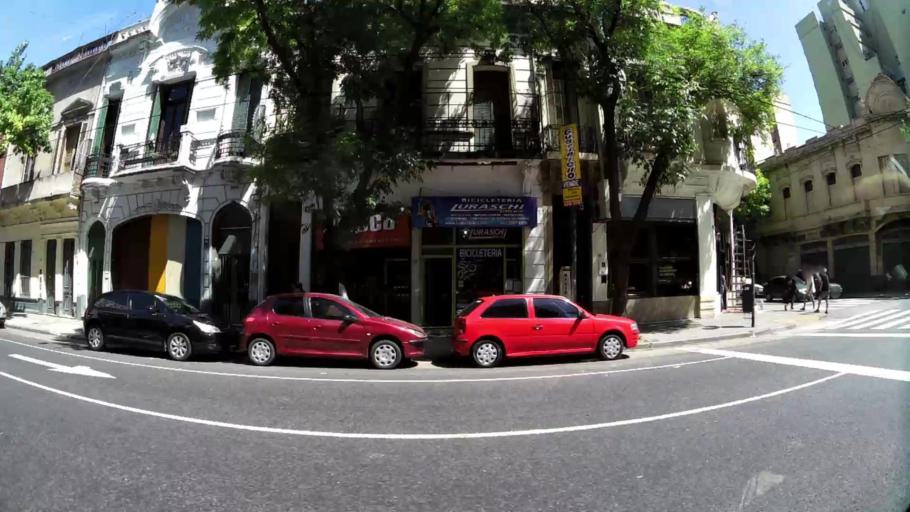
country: AR
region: Buenos Aires F.D.
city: Buenos Aires
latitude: -34.6186
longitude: -58.3975
